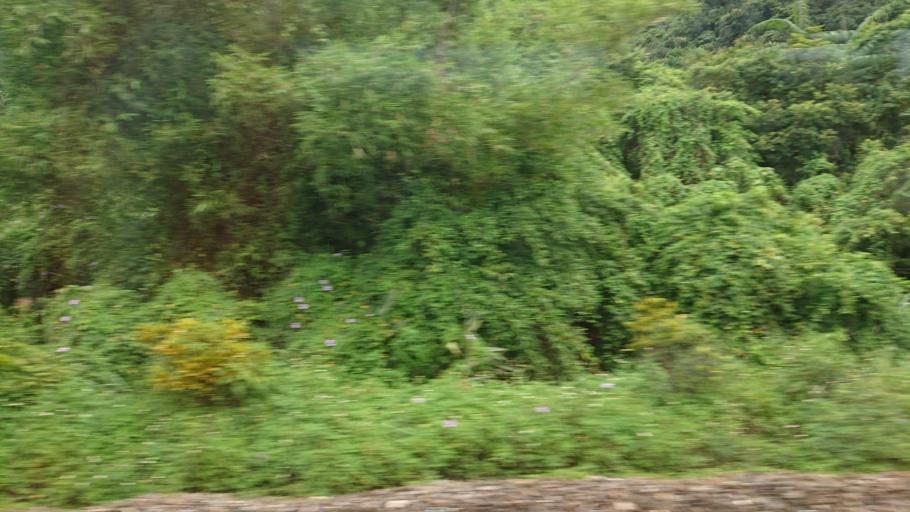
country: TW
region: Taiwan
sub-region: Keelung
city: Keelung
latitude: 24.9474
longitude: 121.9042
